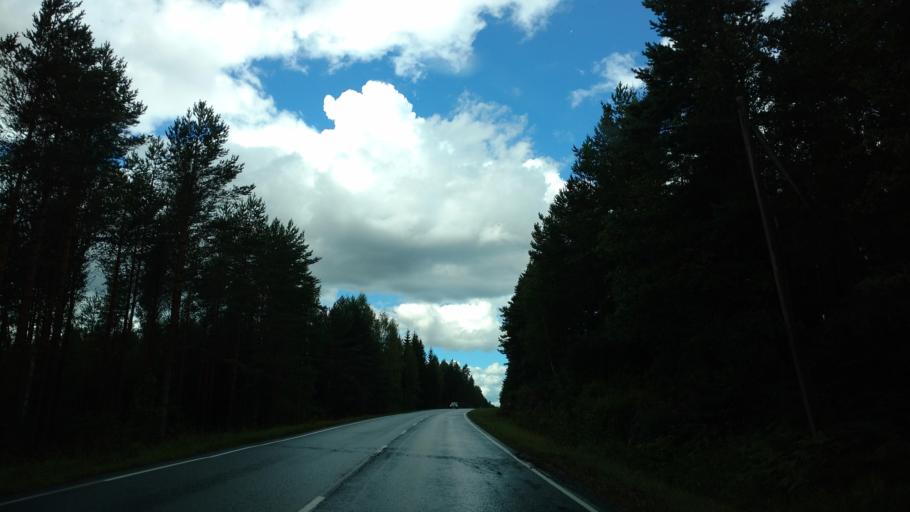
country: FI
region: Varsinais-Suomi
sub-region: Salo
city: Muurla
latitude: 60.2906
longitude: 23.3455
